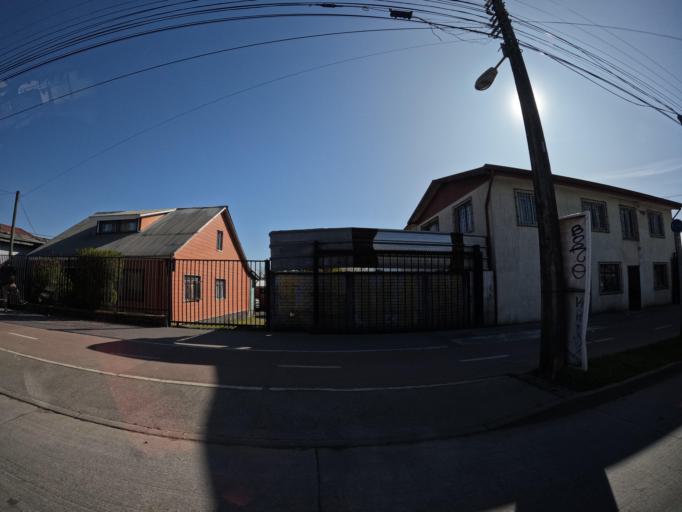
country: CL
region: Biobio
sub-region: Provincia de Concepcion
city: Chiguayante
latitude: -36.9718
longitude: -72.9365
